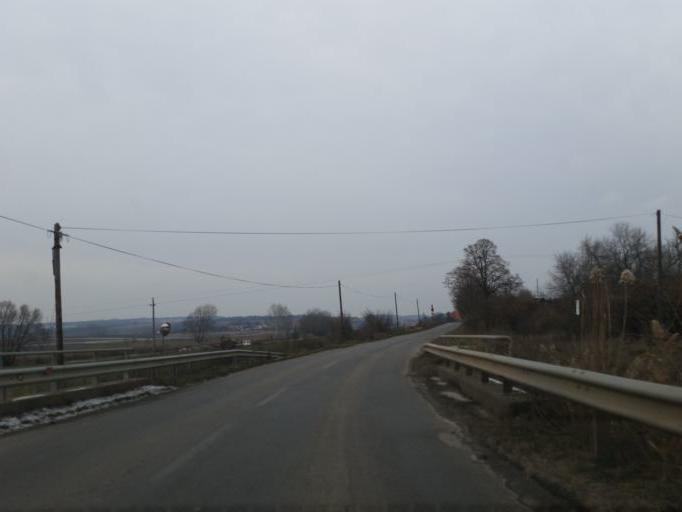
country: HU
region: Pest
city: Perbal
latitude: 47.5813
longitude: 18.7697
